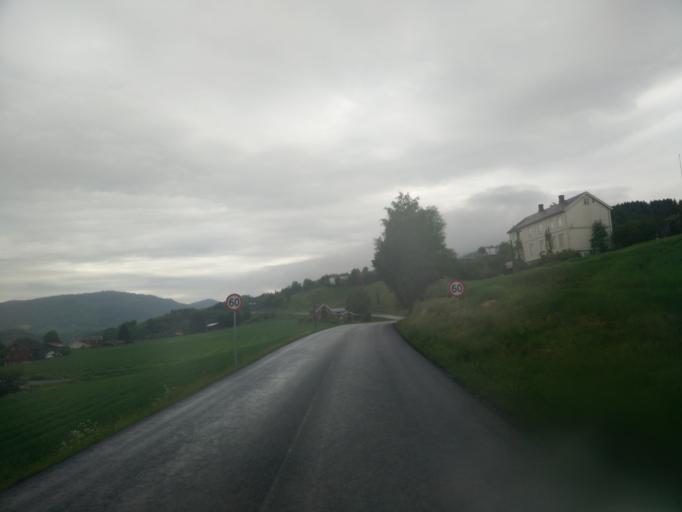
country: NO
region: Sor-Trondelag
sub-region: Orkdal
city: Orkanger
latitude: 63.2605
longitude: 9.7813
